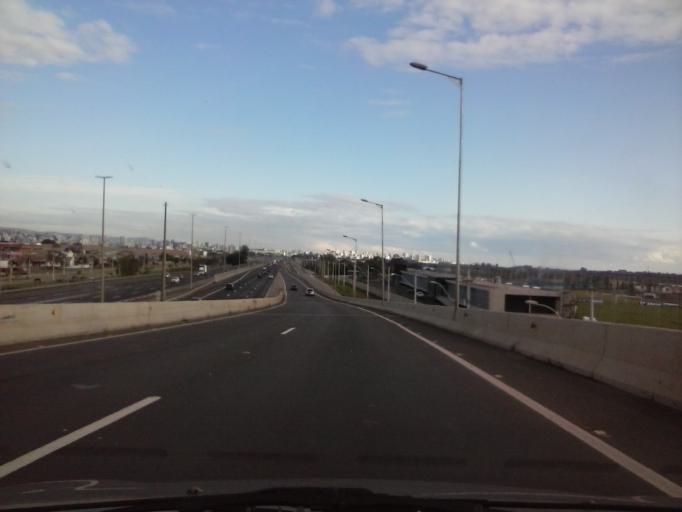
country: BR
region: Rio Grande do Sul
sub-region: Canoas
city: Canoas
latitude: -29.9758
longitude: -51.1998
